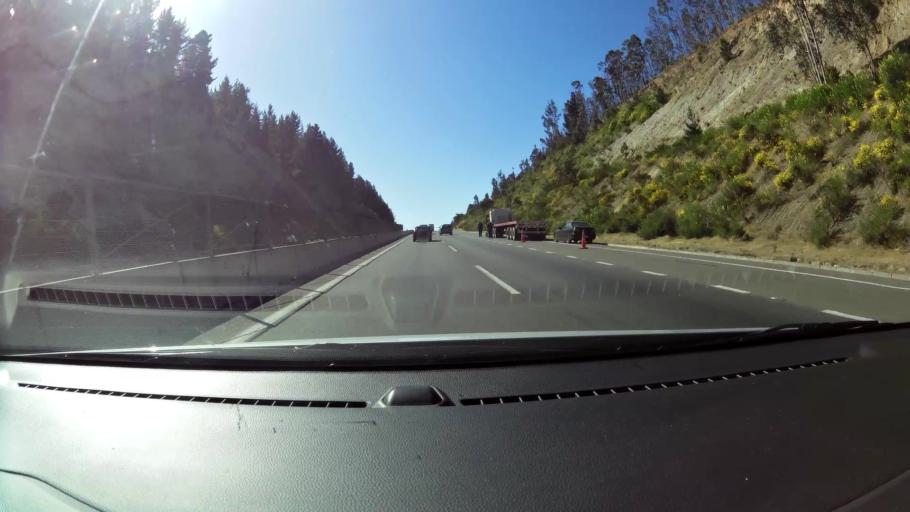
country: CL
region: Valparaiso
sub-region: Provincia de Marga Marga
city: Quilpue
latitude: -33.2067
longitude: -71.4828
